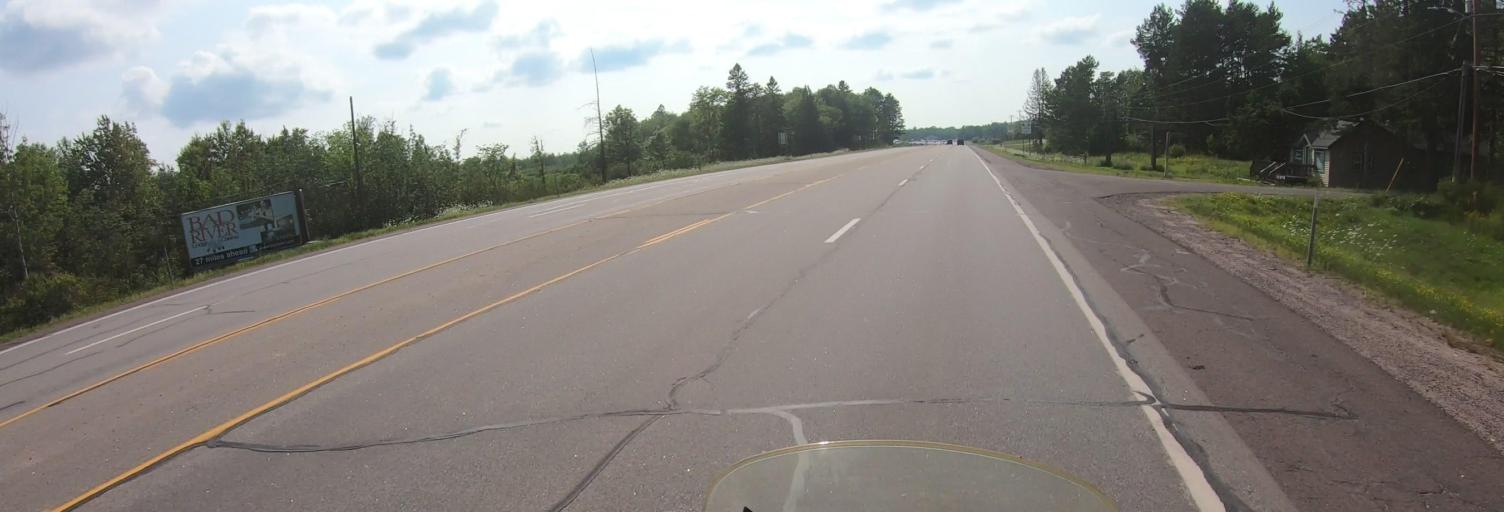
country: US
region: Michigan
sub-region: Gogebic County
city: Bessemer
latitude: 46.4781
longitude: -90.0937
